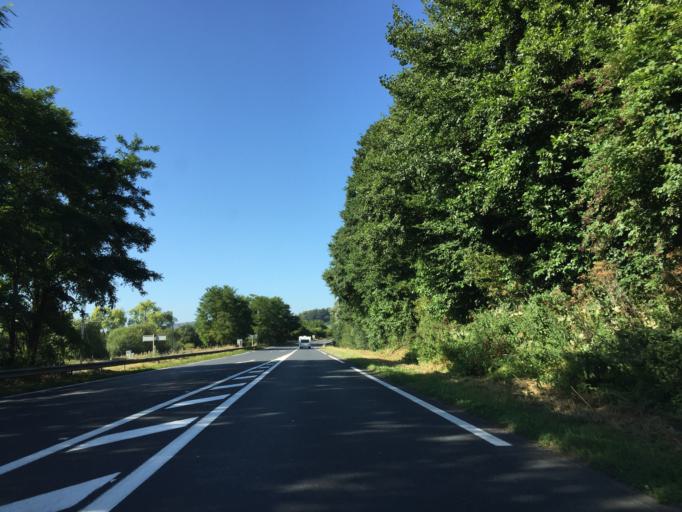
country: FR
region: Lower Normandy
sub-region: Departement du Calvados
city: Saint-Gatien-des-Bois
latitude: 49.2648
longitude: 0.2173
